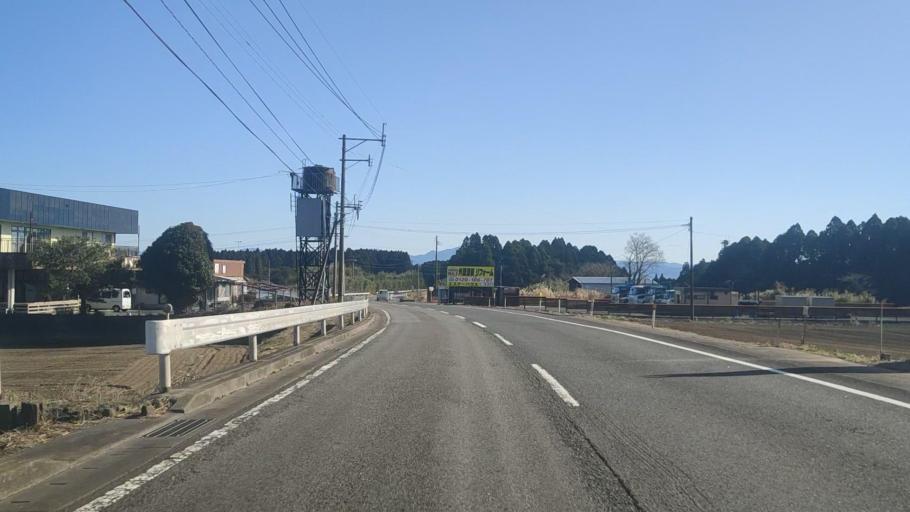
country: JP
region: Kagoshima
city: Sueyoshicho-ninokata
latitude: 31.6881
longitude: 130.9600
